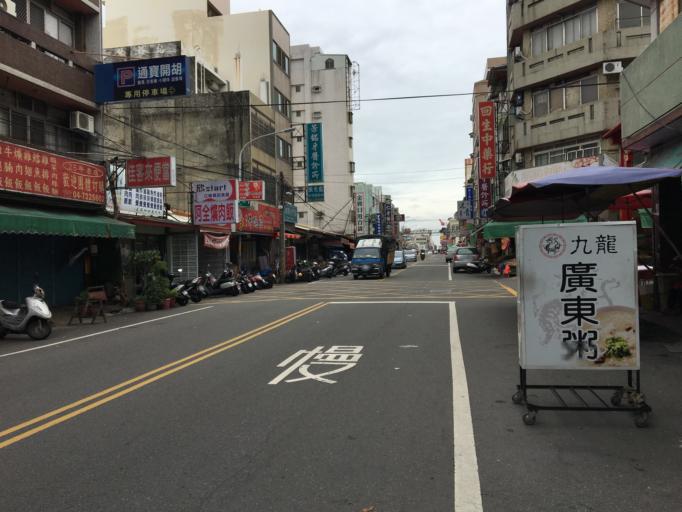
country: TW
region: Taiwan
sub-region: Changhua
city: Chang-hua
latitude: 24.0865
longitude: 120.5450
